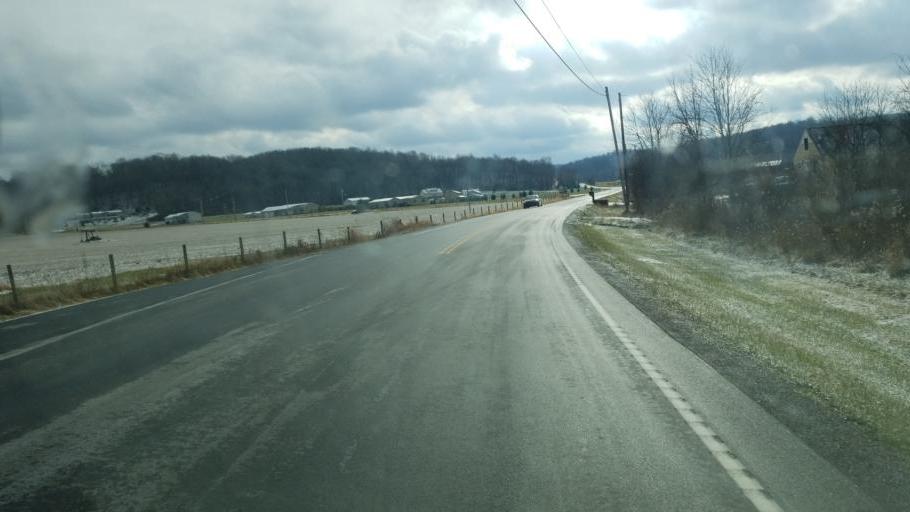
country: US
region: Ohio
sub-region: Muskingum County
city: Frazeysburg
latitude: 40.1343
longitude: -82.1991
